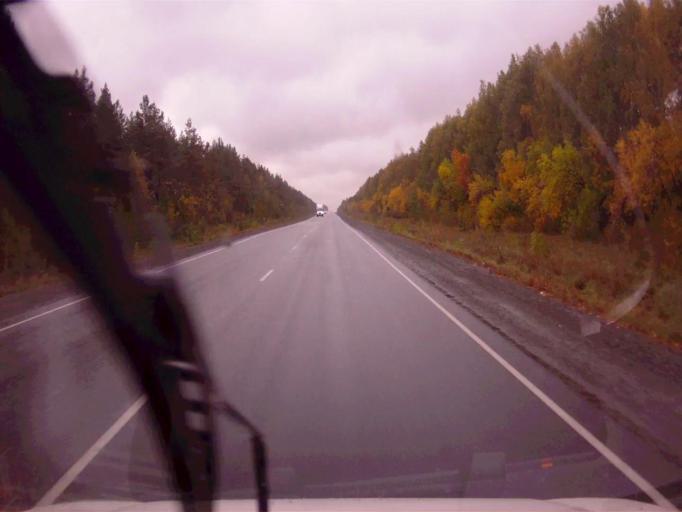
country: RU
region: Chelyabinsk
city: Roshchino
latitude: 55.3749
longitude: 61.1519
